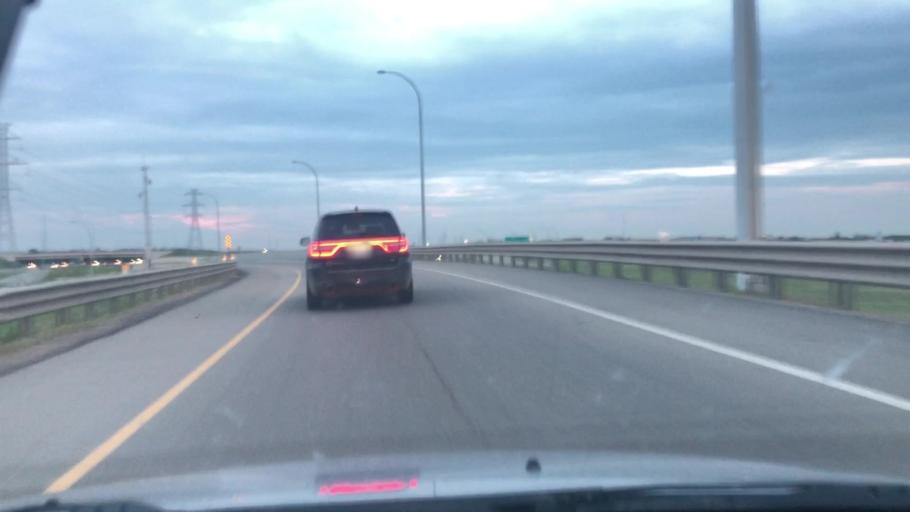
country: CA
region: Alberta
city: St. Albert
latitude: 53.5174
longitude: -113.6568
